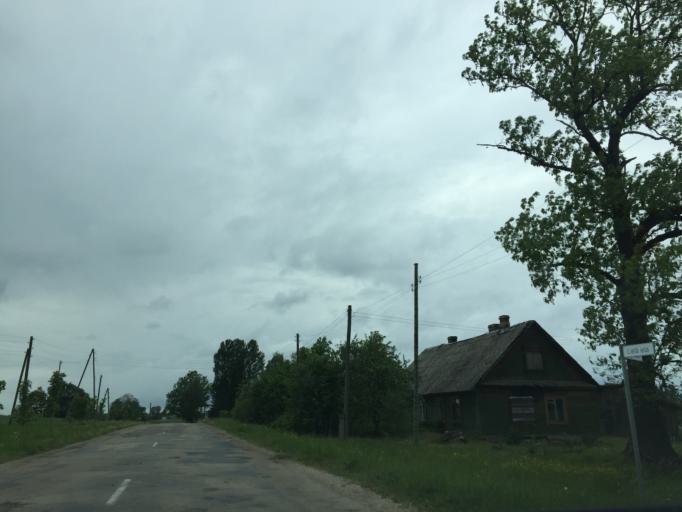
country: LV
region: Varkava
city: Vecvarkava
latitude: 56.0987
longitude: 26.5342
